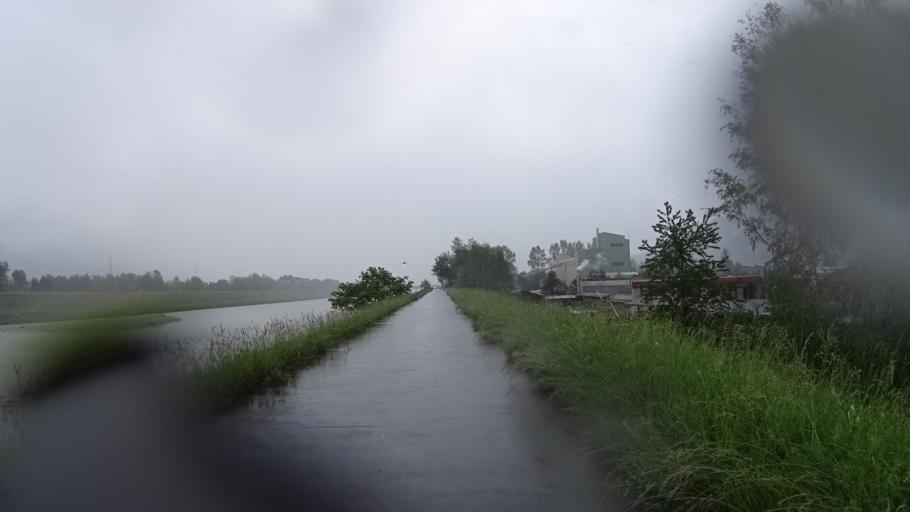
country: LI
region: Triesen
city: Triesen
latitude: 47.1191
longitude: 9.5164
